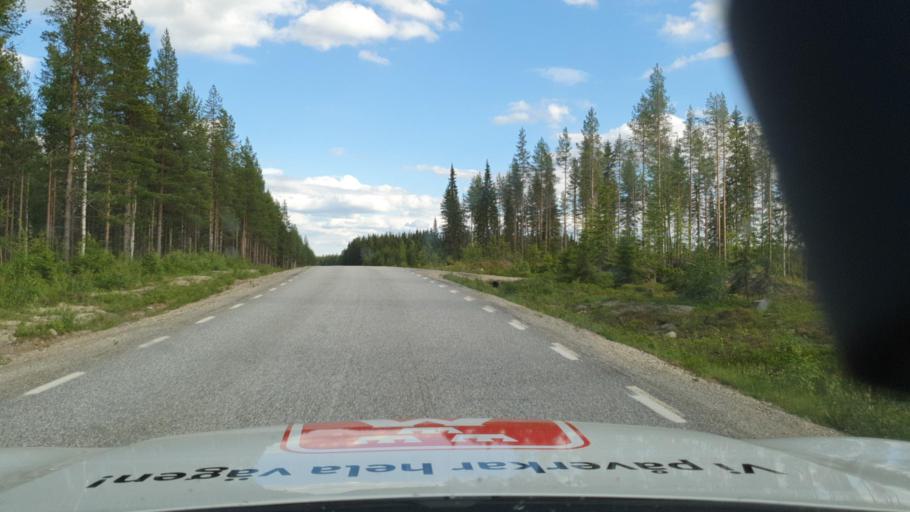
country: SE
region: Vaesterbotten
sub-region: Skelleftea Kommun
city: Langsele
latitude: 64.6996
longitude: 19.9960
